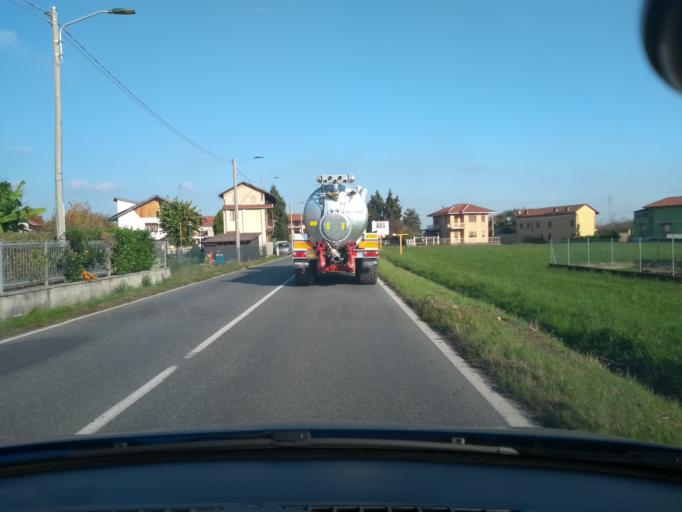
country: IT
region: Piedmont
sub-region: Provincia di Torino
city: Cirie
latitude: 45.2174
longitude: 7.5947
